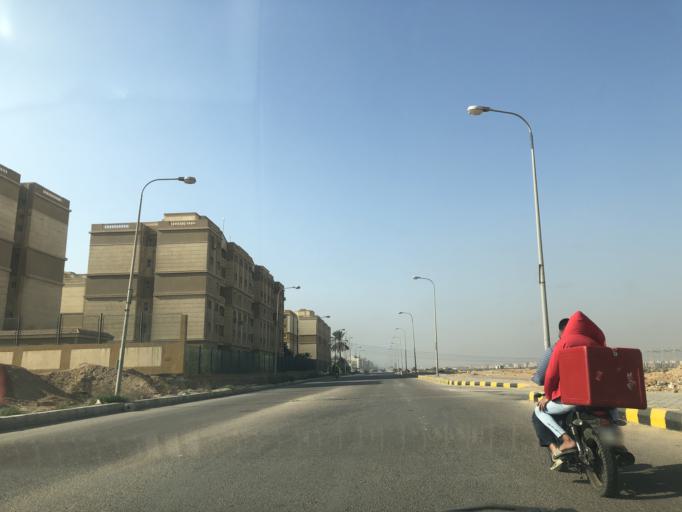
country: EG
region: Al Jizah
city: Madinat Sittah Uktubar
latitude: 29.9193
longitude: 31.0574
